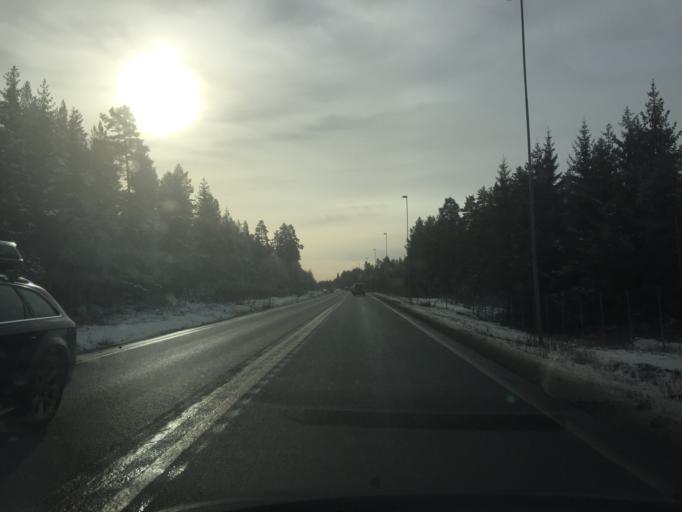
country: NO
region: Hedmark
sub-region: Loten
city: Loten
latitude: 60.7541
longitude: 11.3033
